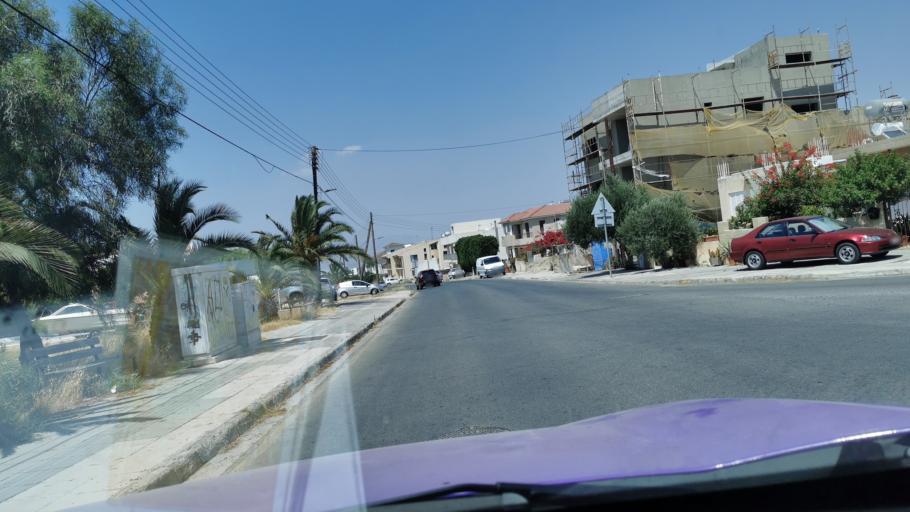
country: CY
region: Lefkosia
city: Kato Deftera
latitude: 35.1213
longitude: 33.2942
